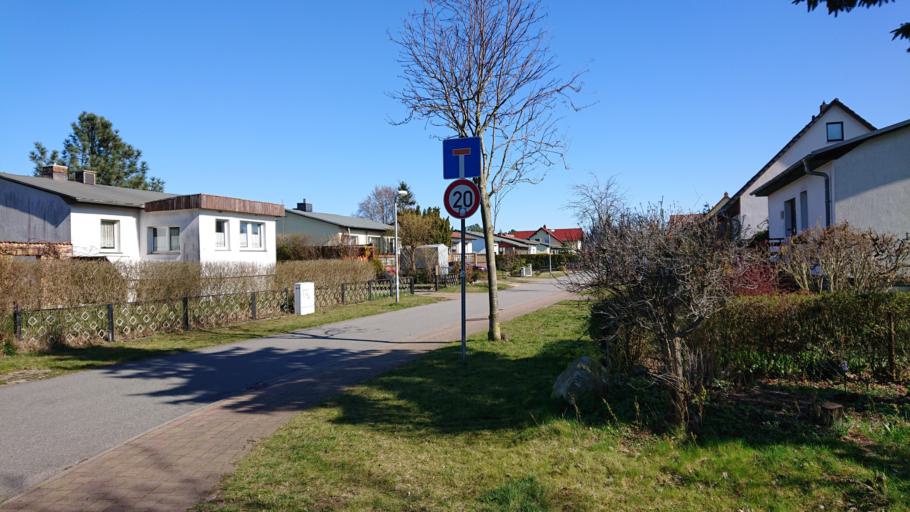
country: DE
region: Mecklenburg-Vorpommern
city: Rovershagen
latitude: 54.1787
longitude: 12.2416
